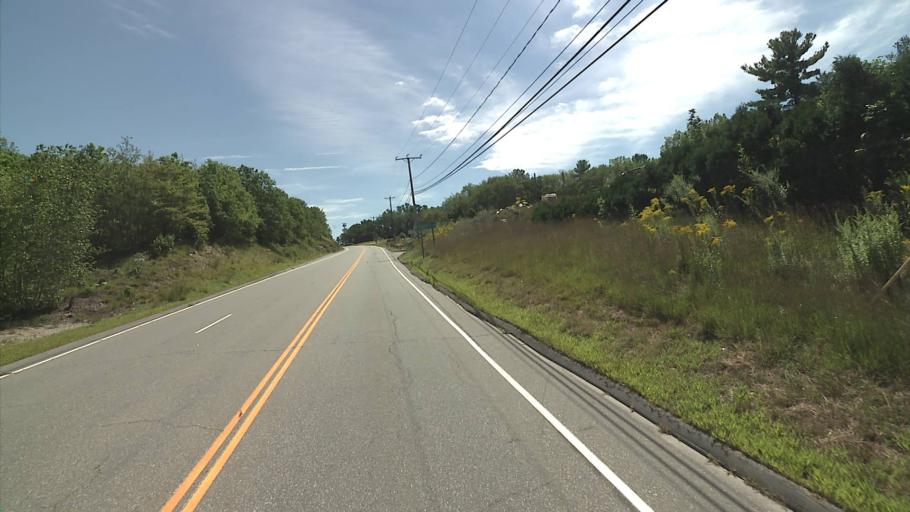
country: US
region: Connecticut
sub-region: Windham County
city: Killingly Center
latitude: 41.8397
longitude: -71.8739
